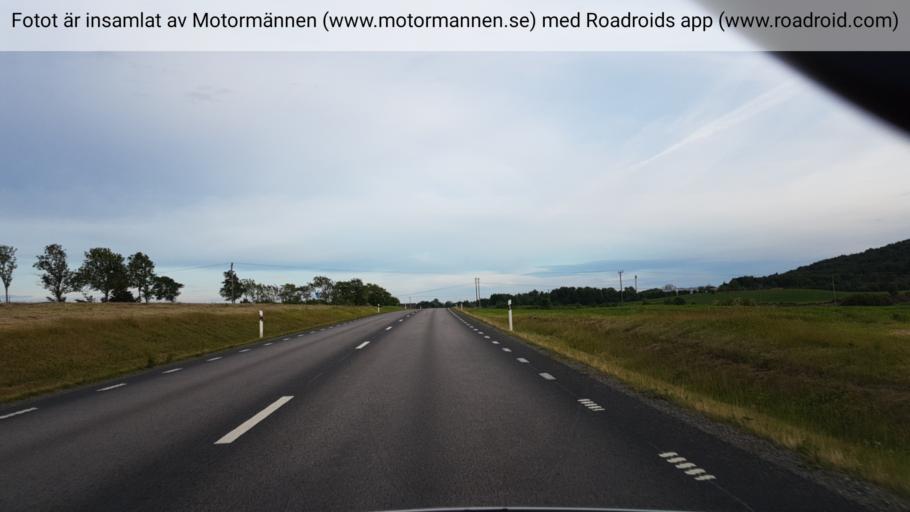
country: SE
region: Vaestra Goetaland
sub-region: Falkopings Kommun
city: Falkoeping
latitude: 58.2007
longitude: 13.5608
